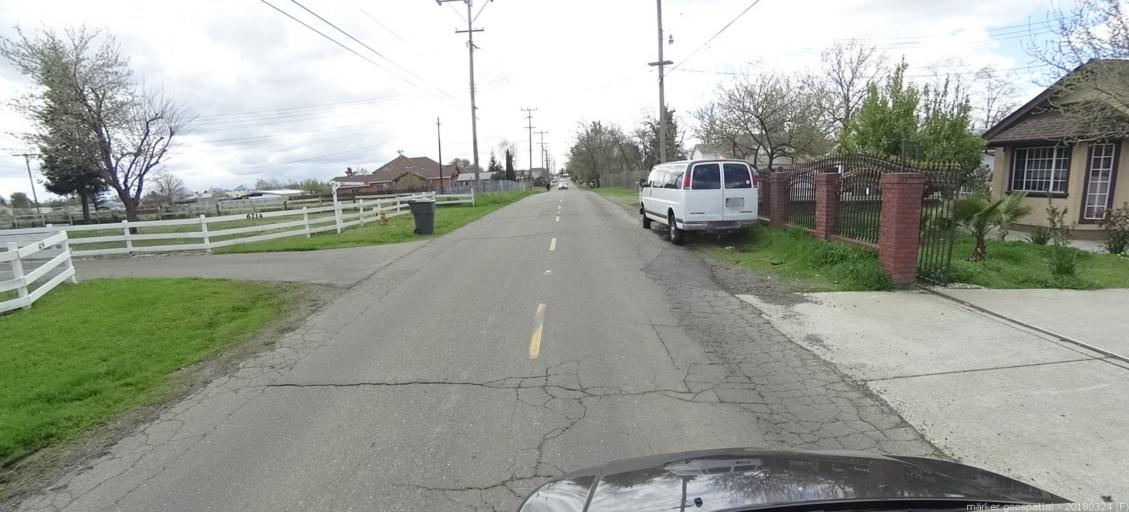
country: US
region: California
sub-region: Sacramento County
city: North Highlands
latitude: 38.6804
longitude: -121.3875
